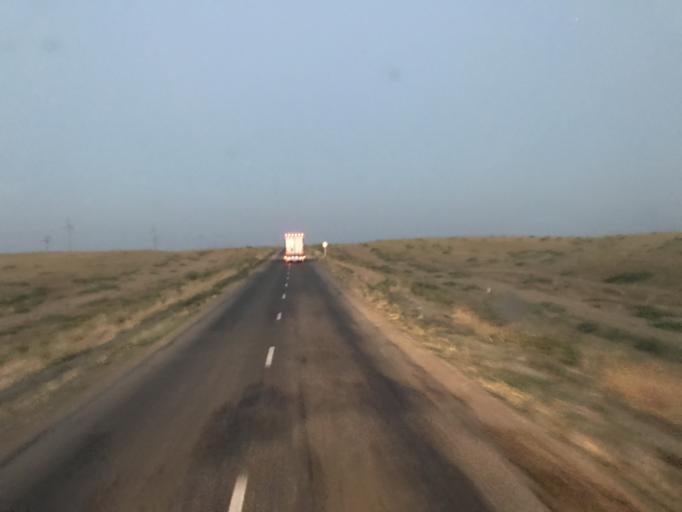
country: UZ
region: Toshkent
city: Chinoz
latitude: 41.1447
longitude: 68.6942
